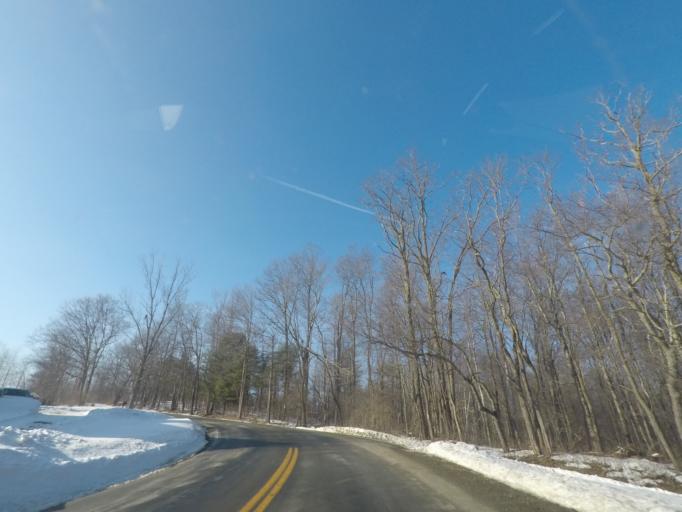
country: US
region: Massachusetts
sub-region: Berkshire County
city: Lanesborough
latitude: 42.5263
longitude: -73.3812
